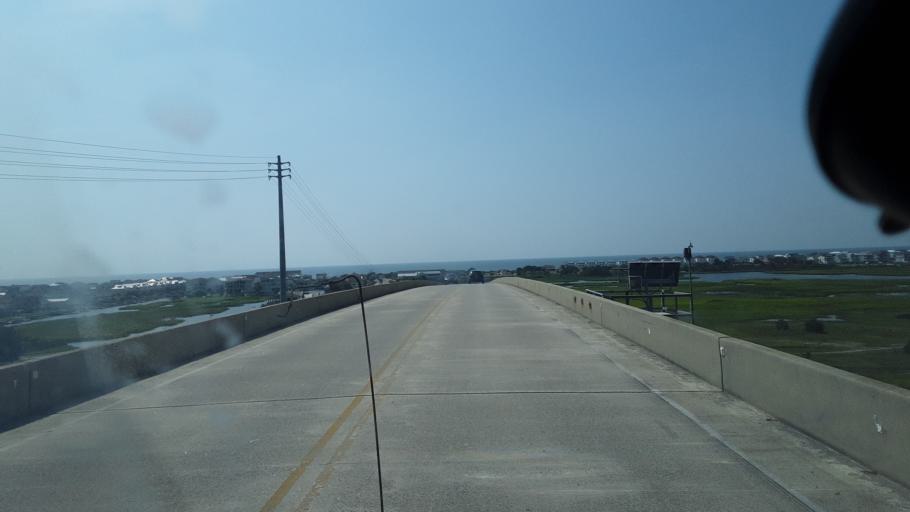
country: US
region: North Carolina
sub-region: Brunswick County
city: Sunset Beach
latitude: 33.8963
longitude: -78.4399
